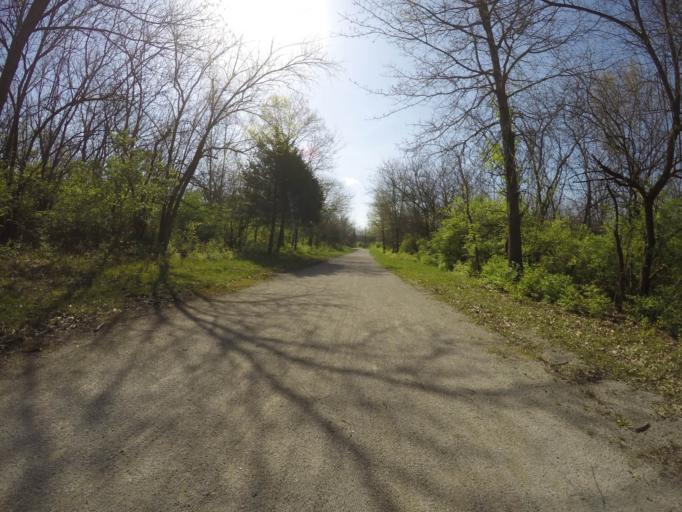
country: US
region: Missouri
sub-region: Jackson County
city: Grandview
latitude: 38.9011
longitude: -94.4880
